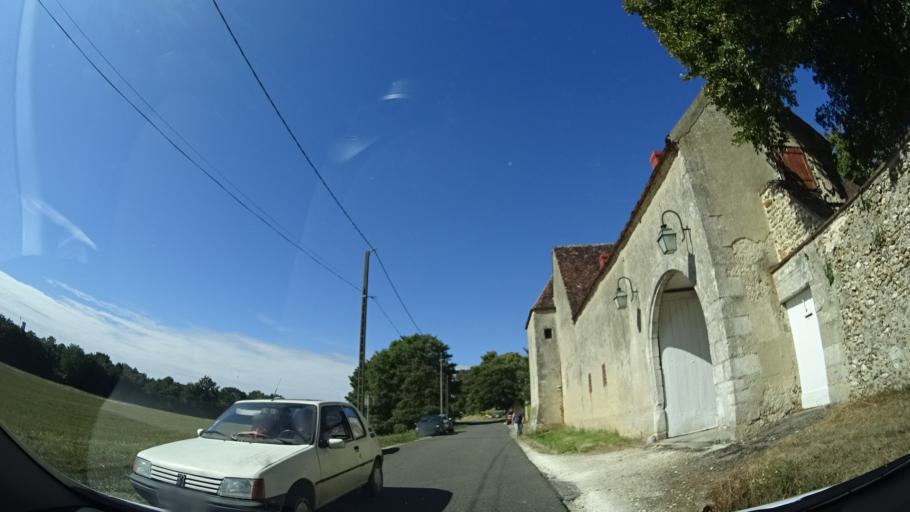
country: FR
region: Centre
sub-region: Departement du Loiret
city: Trigueres
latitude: 47.9414
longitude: 2.9870
